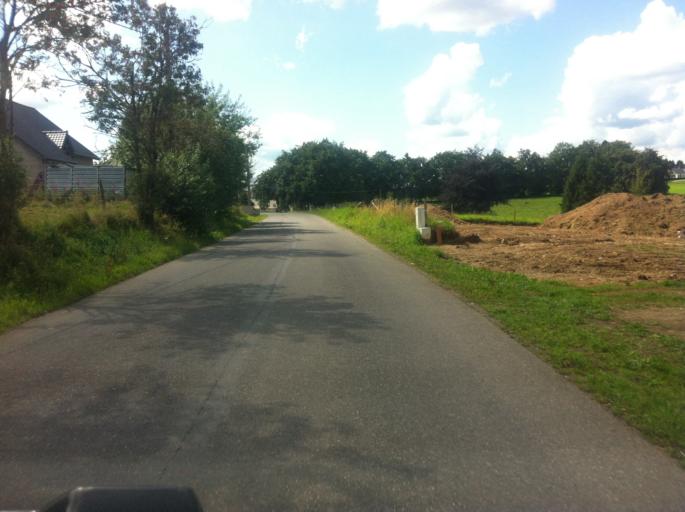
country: DE
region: Rheinland-Pfalz
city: Scheid
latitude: 50.3464
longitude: 6.3468
